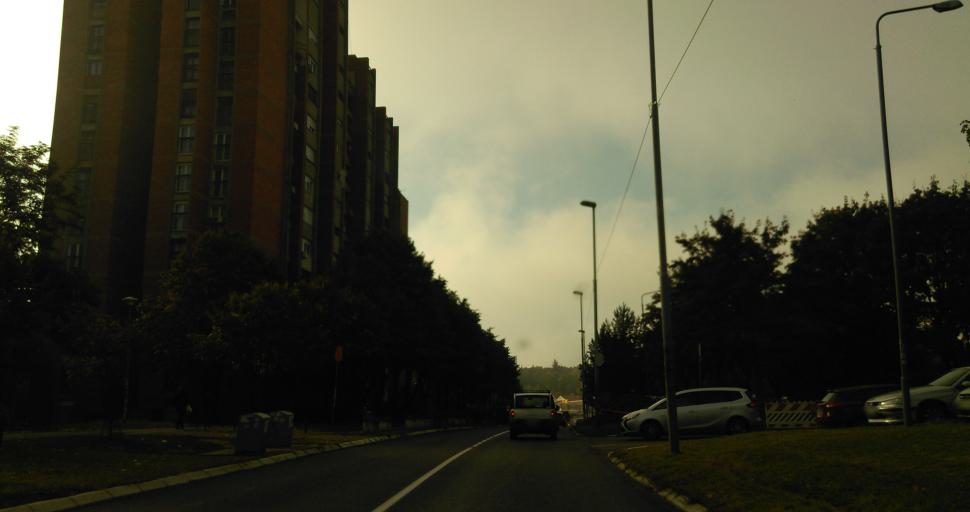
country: RS
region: Central Serbia
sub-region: Belgrade
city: Rakovica
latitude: 44.7338
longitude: 20.4207
